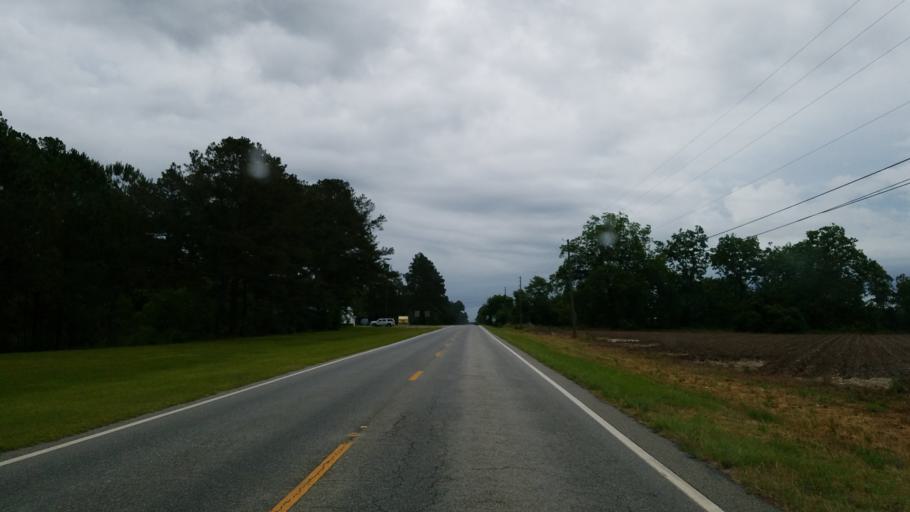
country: US
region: Georgia
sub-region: Berrien County
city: Ray City
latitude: 31.0663
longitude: -83.1692
